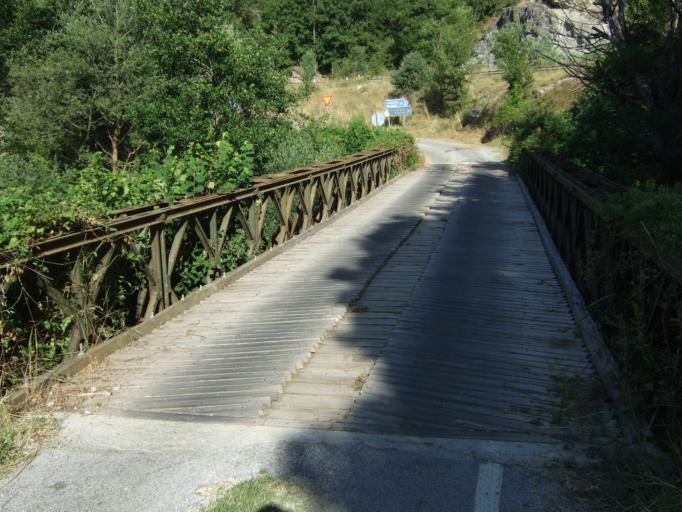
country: GR
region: West Macedonia
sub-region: Nomos Kozanis
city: Tsotili
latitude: 40.1928
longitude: 21.1812
